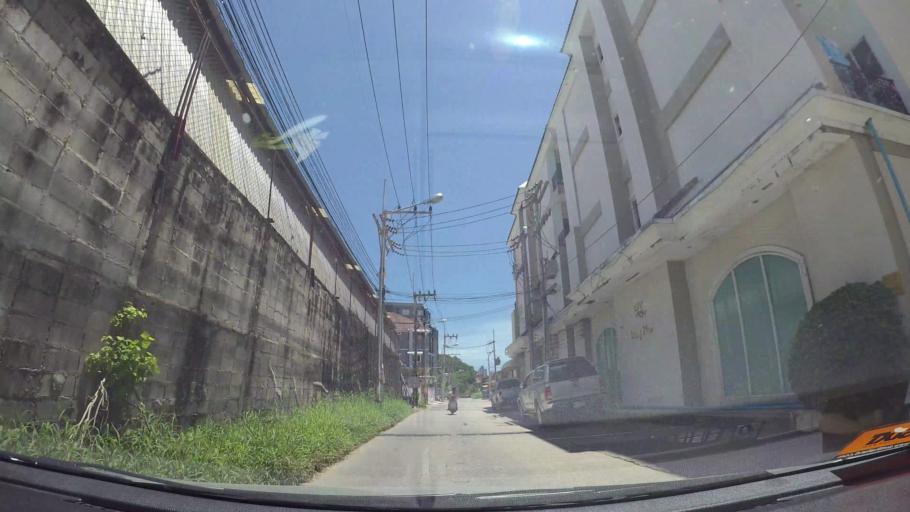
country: TH
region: Chon Buri
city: Phatthaya
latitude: 12.9199
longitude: 100.8933
